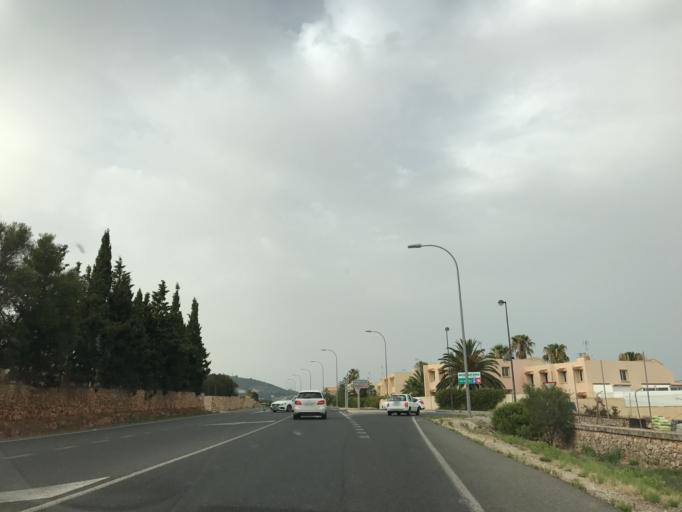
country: ES
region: Balearic Islands
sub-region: Illes Balears
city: Son Servera
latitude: 39.6011
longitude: 3.3690
